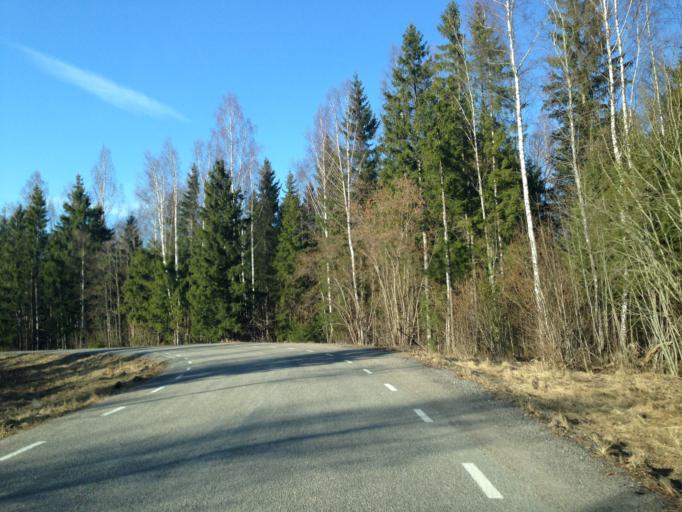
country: EE
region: Harju
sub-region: Nissi vald
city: Turba
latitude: 59.1500
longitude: 24.1514
